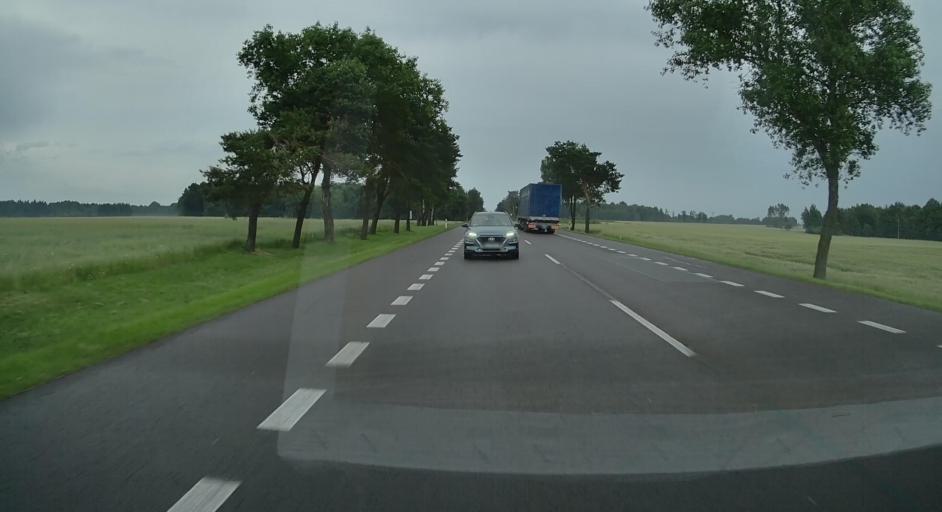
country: PL
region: Lublin Voivodeship
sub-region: Powiat bialski
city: Miedzyrzec Podlaski
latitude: 52.0085
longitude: 22.8311
